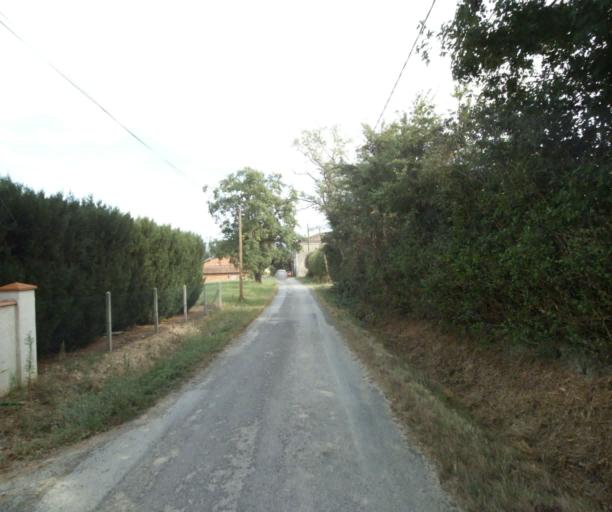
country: FR
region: Midi-Pyrenees
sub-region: Departement du Tarn
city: Soual
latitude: 43.5284
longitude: 2.0609
